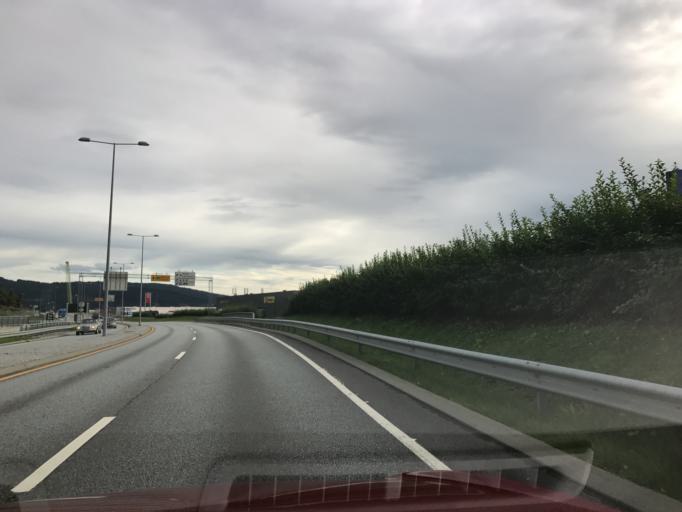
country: NO
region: Hordaland
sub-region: Bergen
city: Hylkje
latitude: 60.4825
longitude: 5.3725
